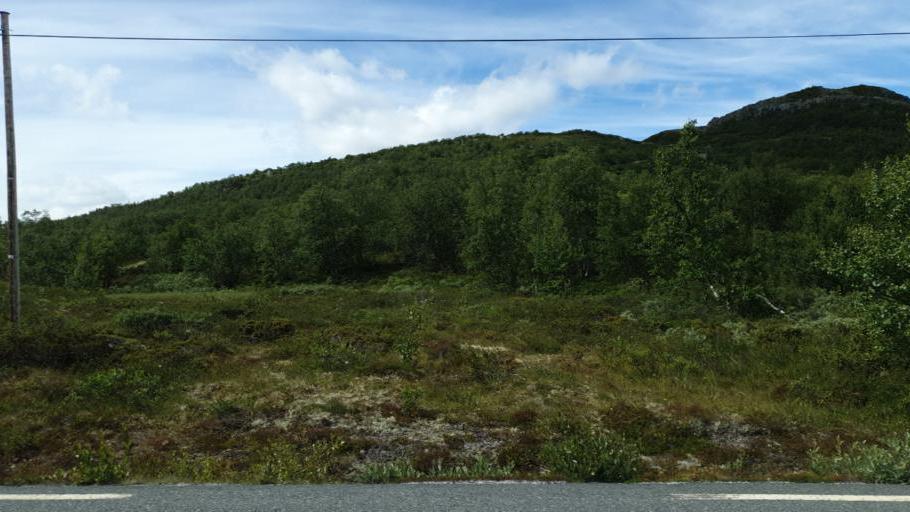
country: NO
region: Oppland
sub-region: Oystre Slidre
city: Heggenes
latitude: 61.4986
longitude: 8.8439
